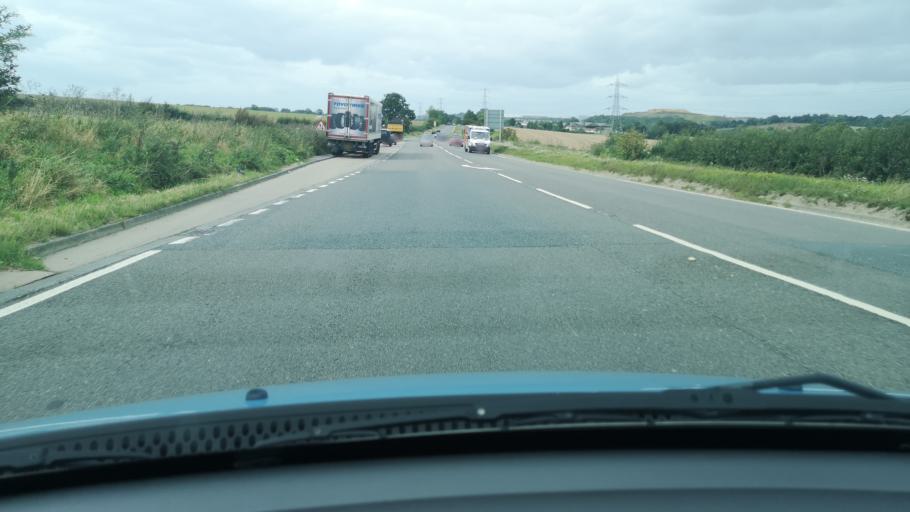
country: GB
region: England
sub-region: Doncaster
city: Marr
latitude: 53.5818
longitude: -1.2259
